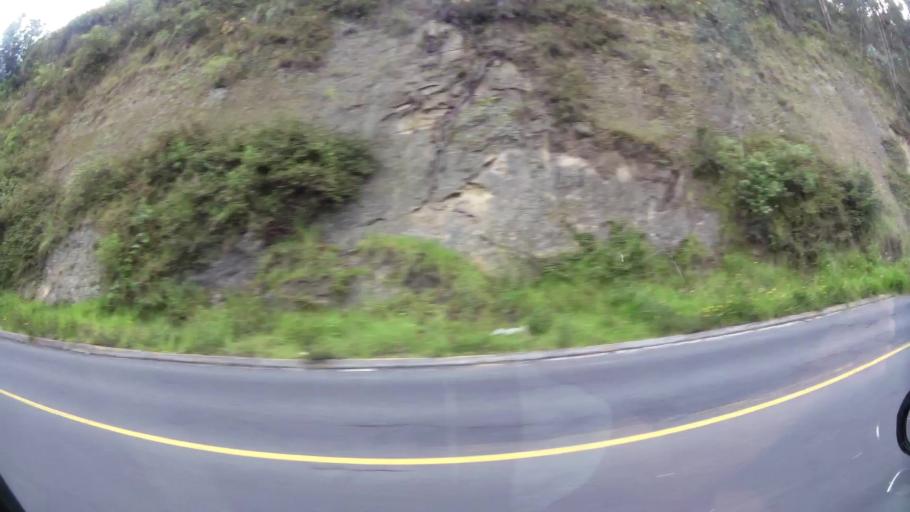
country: EC
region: Pichincha
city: Quito
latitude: -0.2678
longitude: -78.4964
